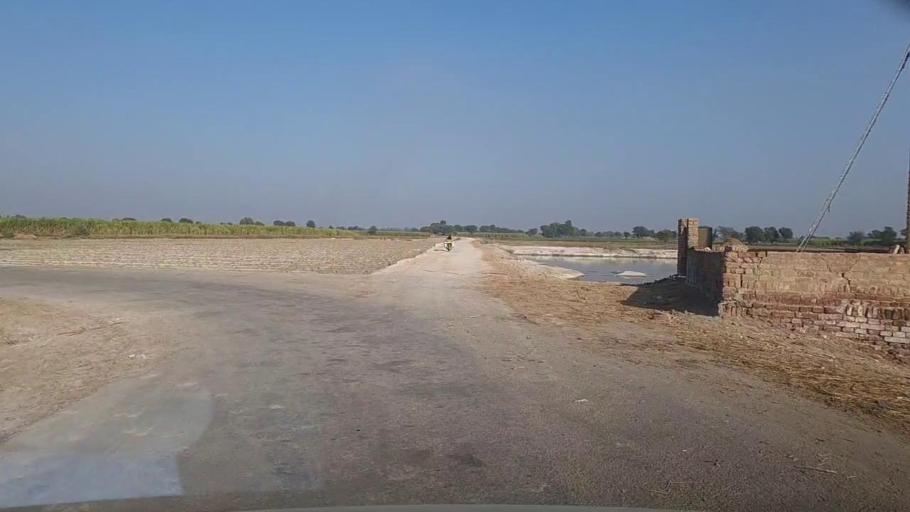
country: PK
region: Sindh
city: Dadu
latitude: 26.8460
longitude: 67.7935
